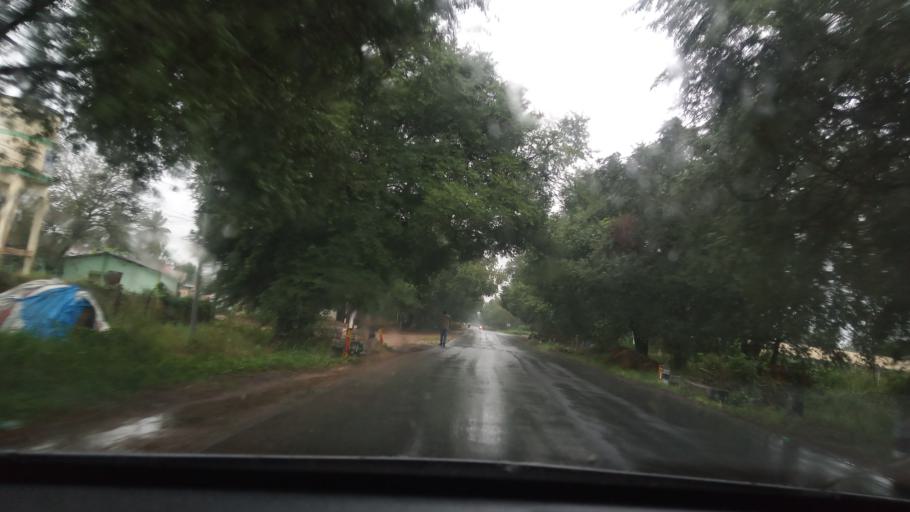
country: IN
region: Tamil Nadu
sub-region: Vellore
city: Walajapet
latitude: 12.8493
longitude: 79.3904
